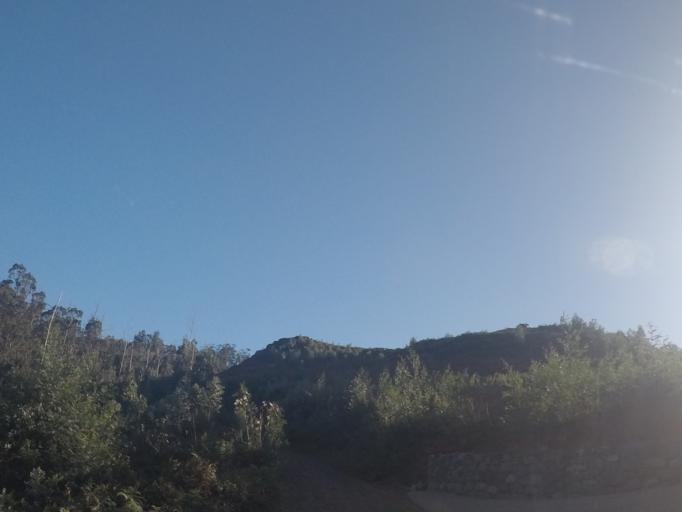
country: PT
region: Madeira
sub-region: Funchal
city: Nossa Senhora do Monte
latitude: 32.6747
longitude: -16.8804
